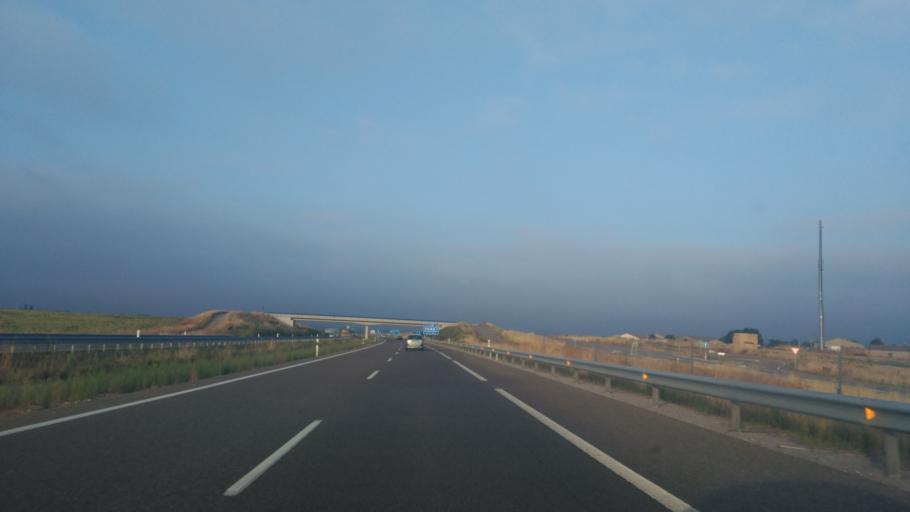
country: ES
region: Castille and Leon
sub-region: Provincia de Salamanca
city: Robliza de Cojos
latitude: 40.8830
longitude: -5.9640
